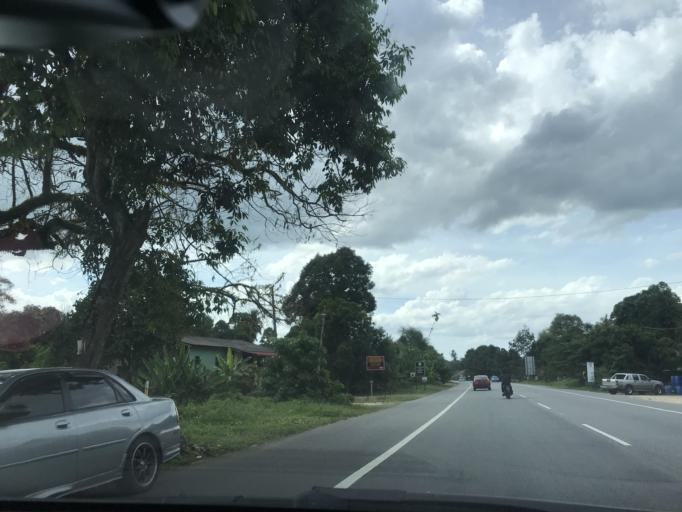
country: MY
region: Kelantan
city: Kampong Pangkal Kalong
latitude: 5.9370
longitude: 102.1919
